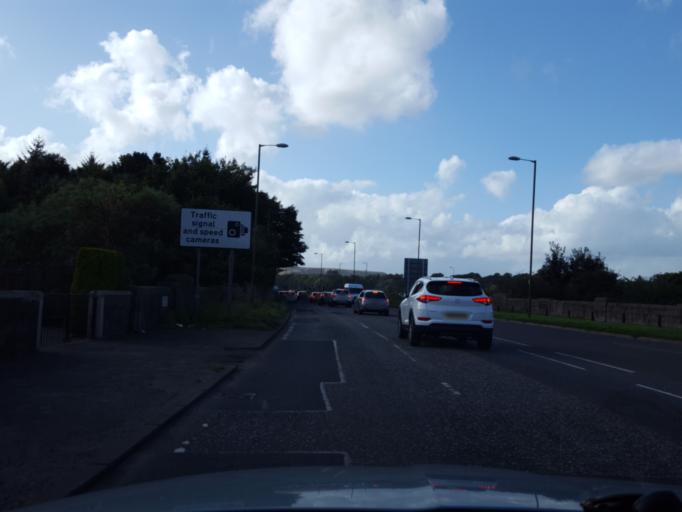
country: GB
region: Scotland
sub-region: Edinburgh
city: Newbridge
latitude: 55.9407
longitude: -3.4091
